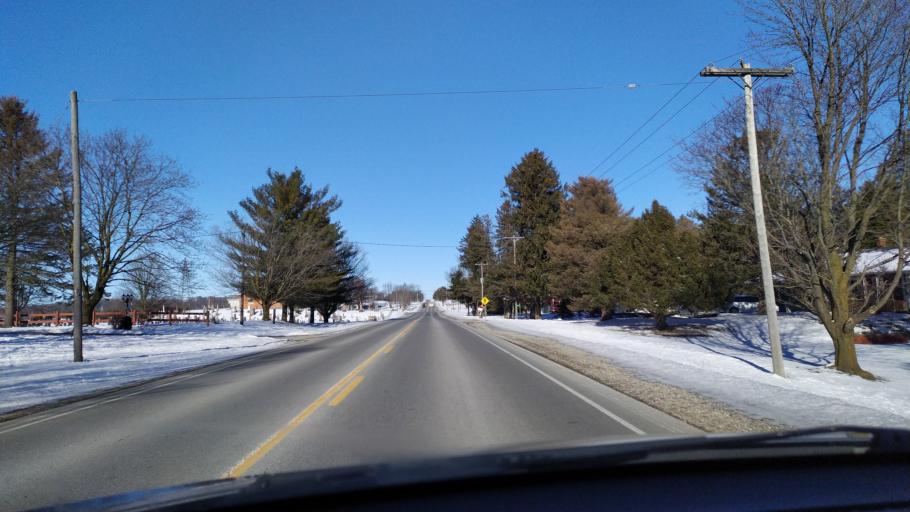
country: CA
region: Ontario
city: Stratford
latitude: 43.3859
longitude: -80.8372
